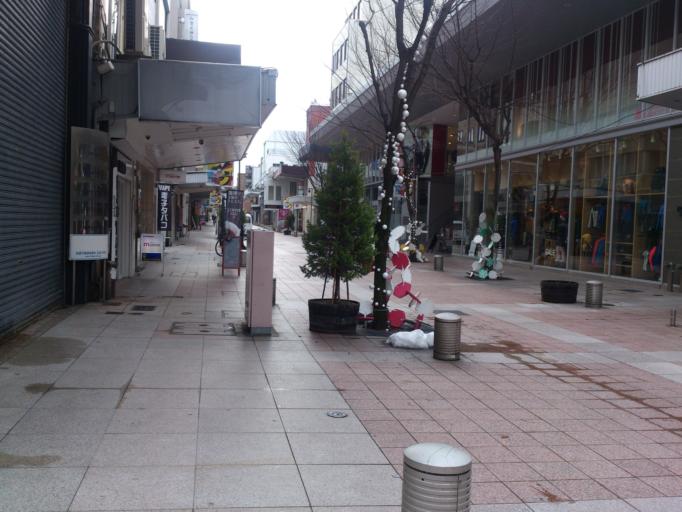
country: JP
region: Ishikawa
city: Kanazawa-shi
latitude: 36.5597
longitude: 136.6542
